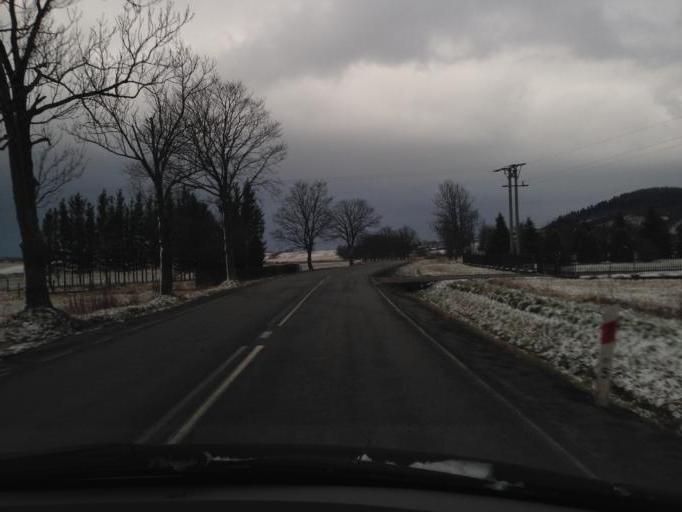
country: PL
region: Subcarpathian Voivodeship
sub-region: Powiat jasielski
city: Osiek Jasielski
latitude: 49.6115
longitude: 21.4789
